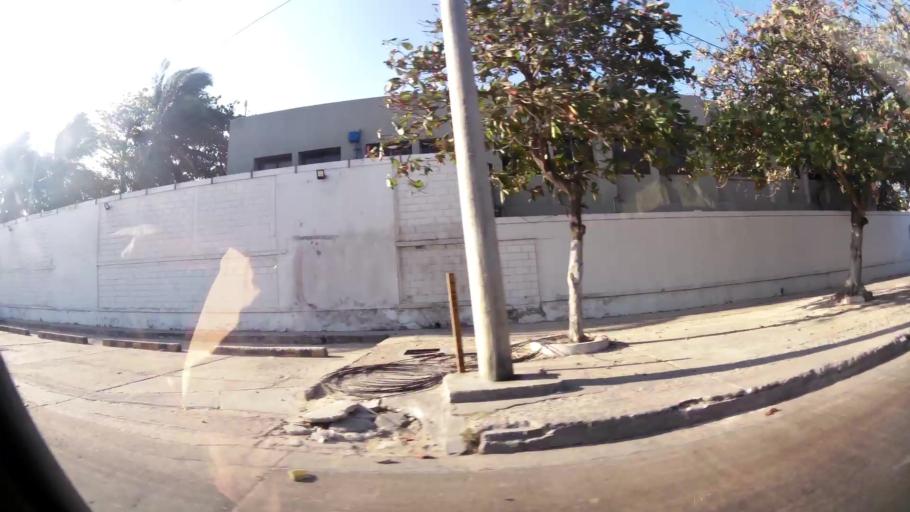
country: CO
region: Atlantico
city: Barranquilla
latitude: 11.0386
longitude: -74.8224
